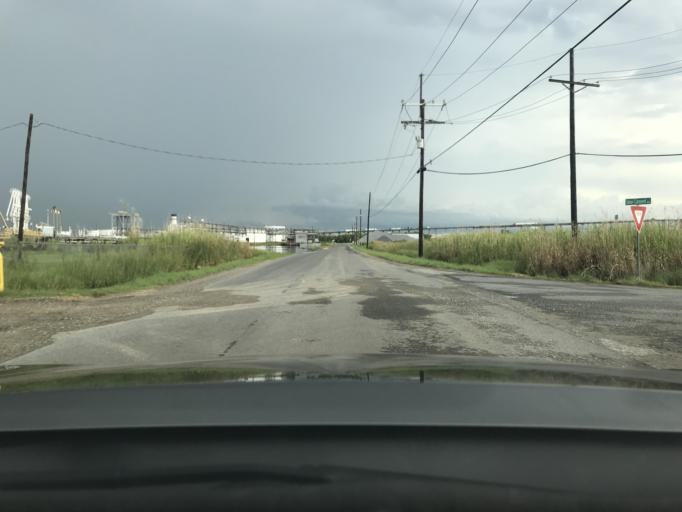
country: US
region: Louisiana
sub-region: Calcasieu Parish
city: Westlake
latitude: 30.2275
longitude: -93.2515
